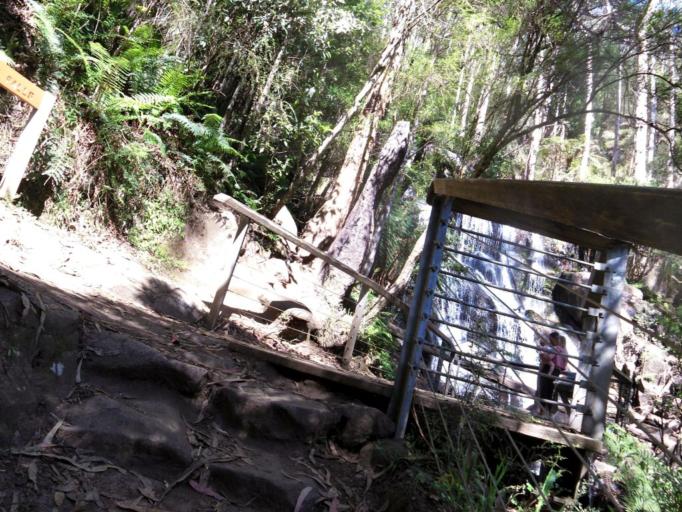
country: AU
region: Victoria
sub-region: Baw Baw
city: Warragul
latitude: -37.8480
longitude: 146.0496
